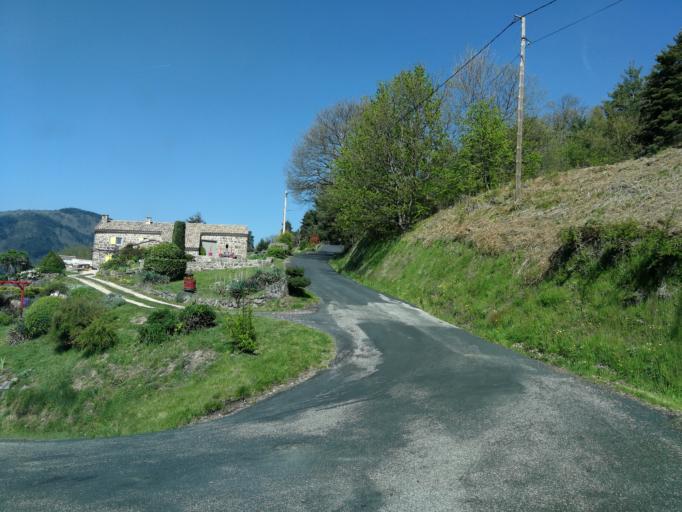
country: FR
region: Rhone-Alpes
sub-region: Departement de l'Ardeche
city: Le Cheylard
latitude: 44.9231
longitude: 4.4195
